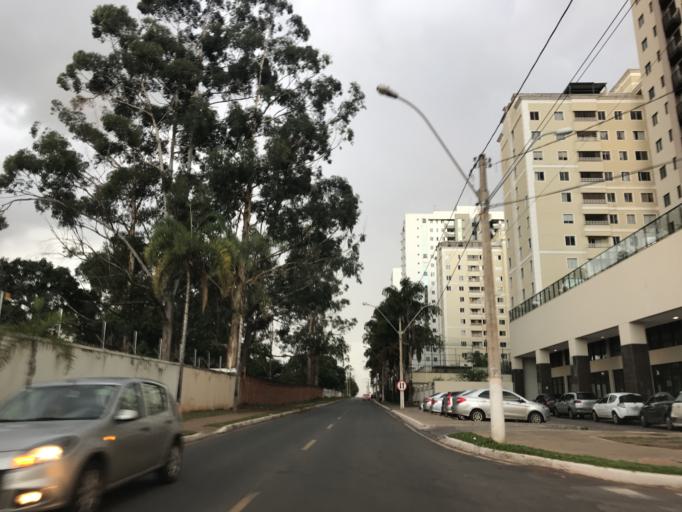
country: BR
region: Federal District
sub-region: Brasilia
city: Brasilia
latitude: -15.8305
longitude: -48.0101
